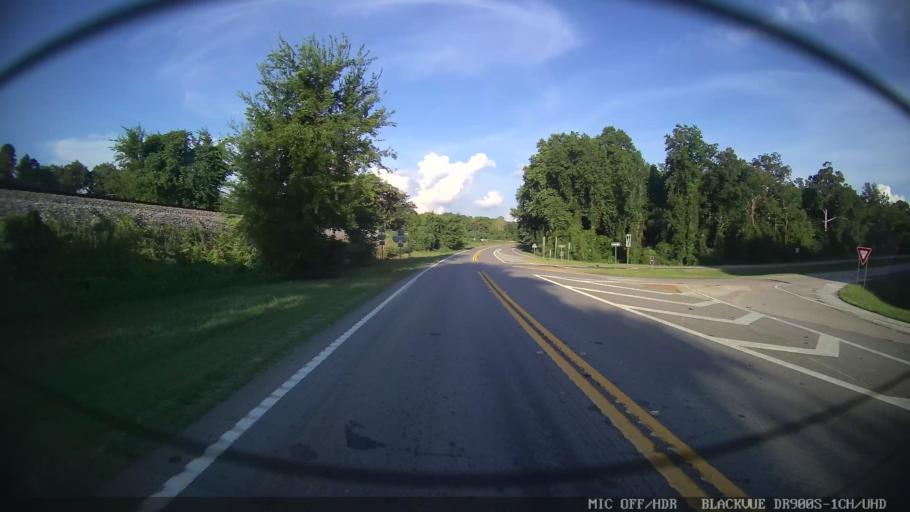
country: US
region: Georgia
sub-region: Monroe County
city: Forsyth
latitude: 32.9517
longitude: -83.8208
